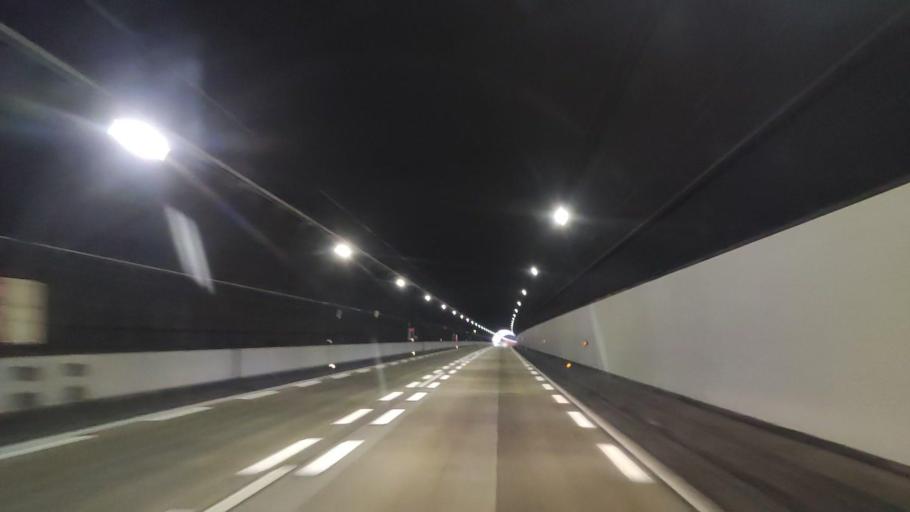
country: JP
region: Hiroshima
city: Fukuyama
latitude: 34.5069
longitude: 133.3314
